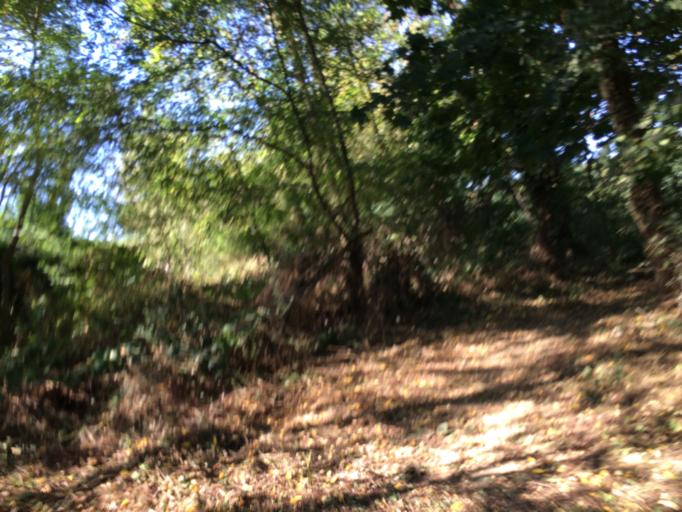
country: FR
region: Ile-de-France
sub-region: Departement de l'Essonne
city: Gometz-le-Chatel
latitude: 48.6755
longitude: 2.1470
